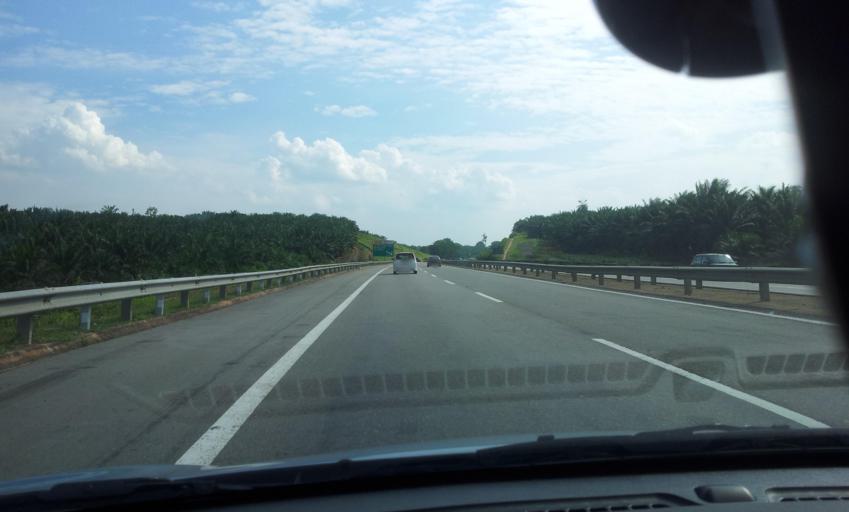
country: MY
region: Pahang
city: Temerluh
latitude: 3.5517
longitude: 102.5419
